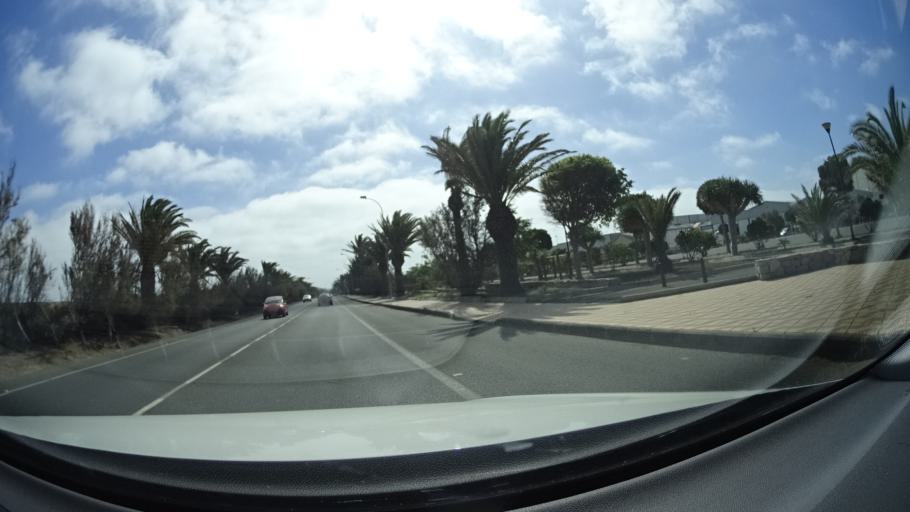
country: ES
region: Canary Islands
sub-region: Provincia de Las Palmas
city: Cruce de Arinaga
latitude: 27.8612
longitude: -15.4022
